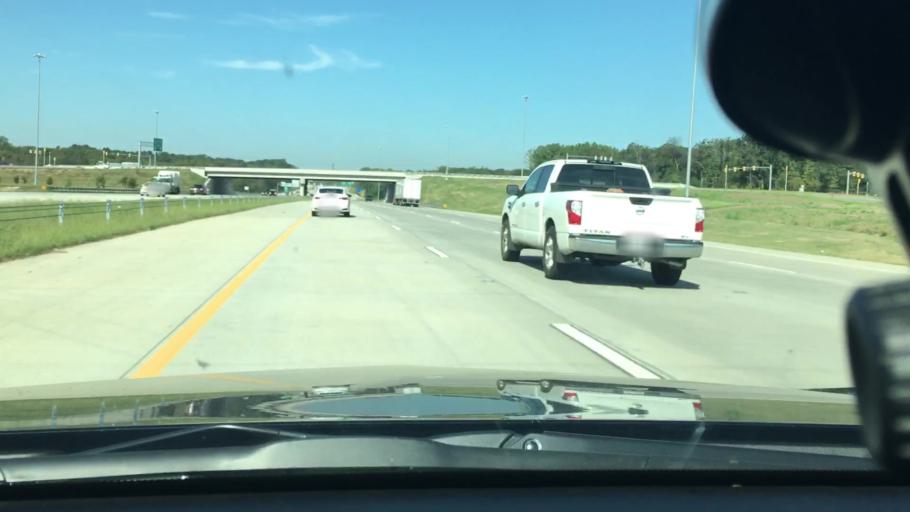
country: US
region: North Carolina
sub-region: Cabarrus County
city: Harrisburg
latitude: 35.3610
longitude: -80.7466
